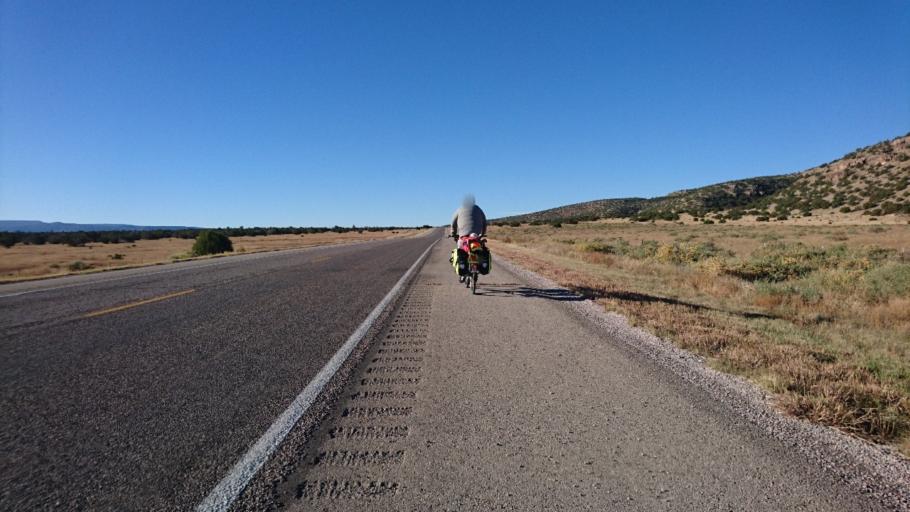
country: US
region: New Mexico
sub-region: Cibola County
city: Grants
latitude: 34.9855
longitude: -107.9036
